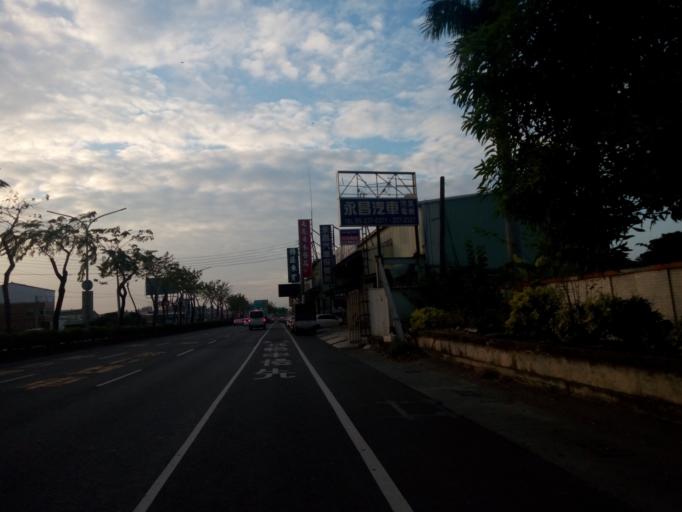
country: TW
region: Taiwan
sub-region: Chiayi
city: Jiayi Shi
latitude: 23.4913
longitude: 120.4004
